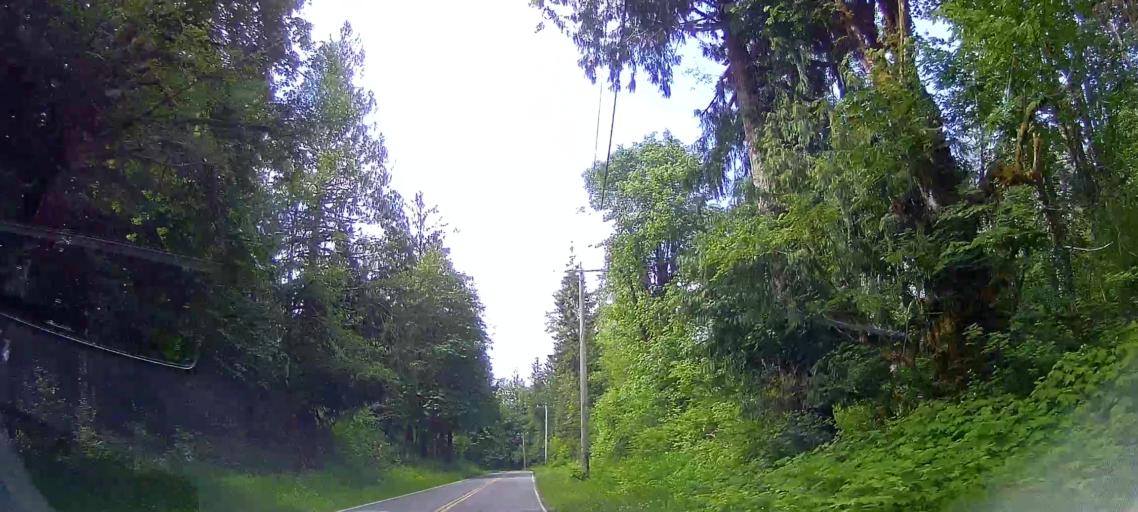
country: US
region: Washington
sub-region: Skagit County
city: Sedro-Woolley
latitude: 48.6738
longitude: -122.1535
